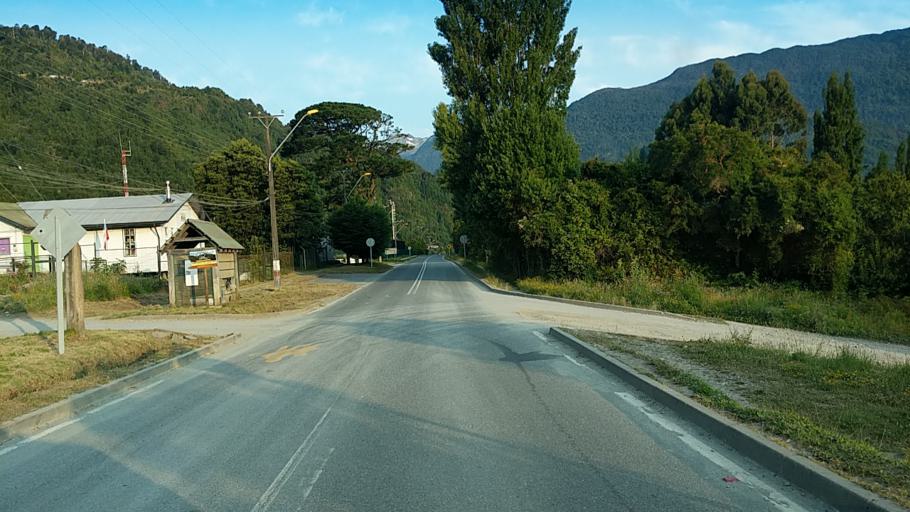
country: CL
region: Los Lagos
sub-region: Provincia de Llanquihue
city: La Ensenada
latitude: -41.4932
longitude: -72.3049
